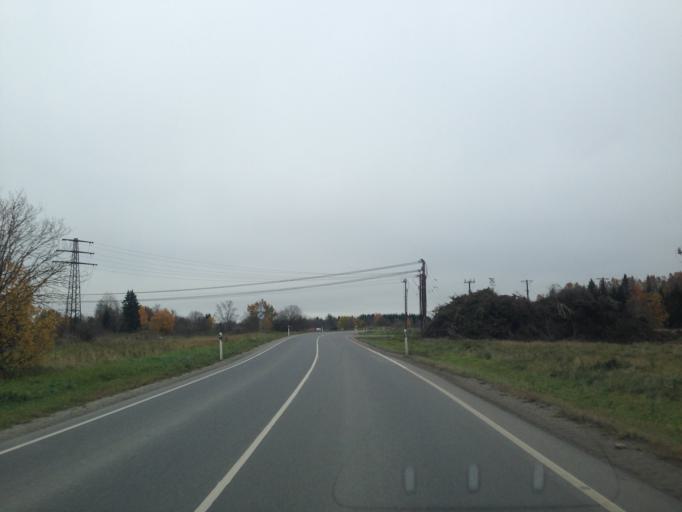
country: EE
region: Harju
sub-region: Harku vald
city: Tabasalu
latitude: 59.4147
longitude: 24.5441
